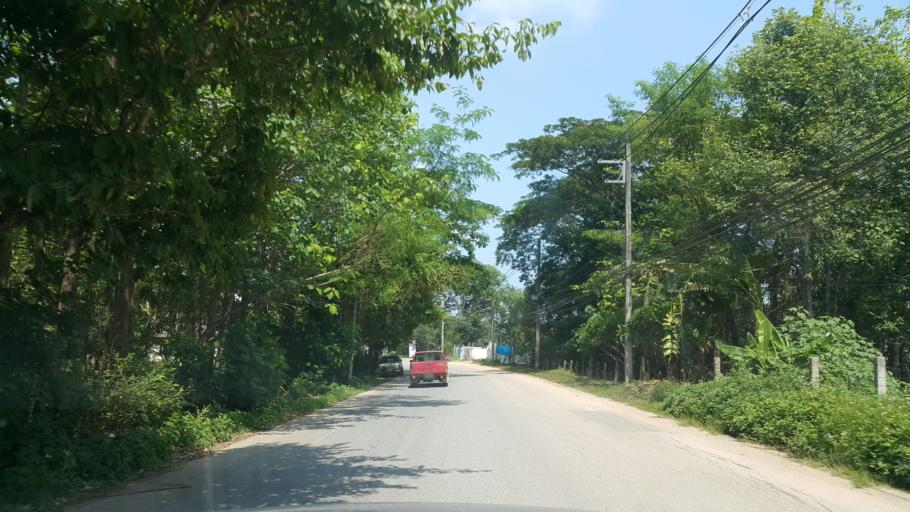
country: TH
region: Chiang Rai
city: Chiang Rai
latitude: 19.9317
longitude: 99.8157
